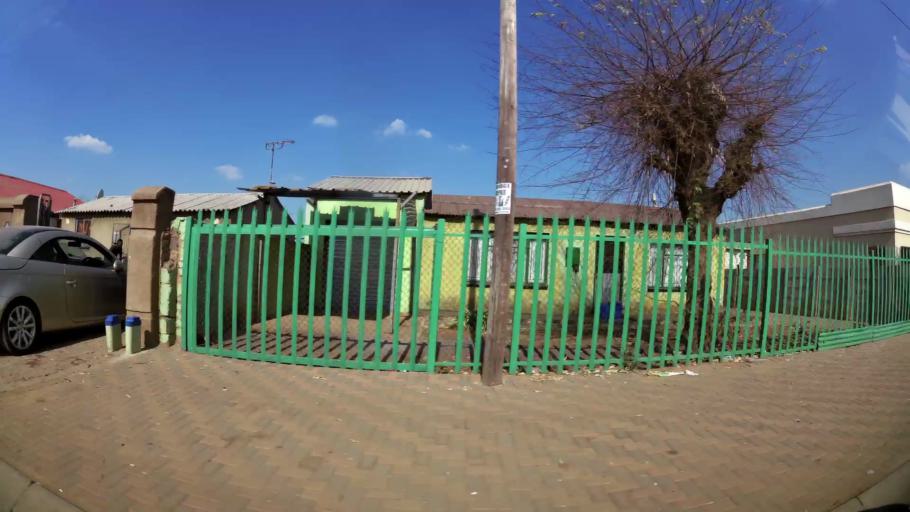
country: ZA
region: Gauteng
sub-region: Ekurhuleni Metropolitan Municipality
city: Brakpan
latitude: -26.1515
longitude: 28.4104
